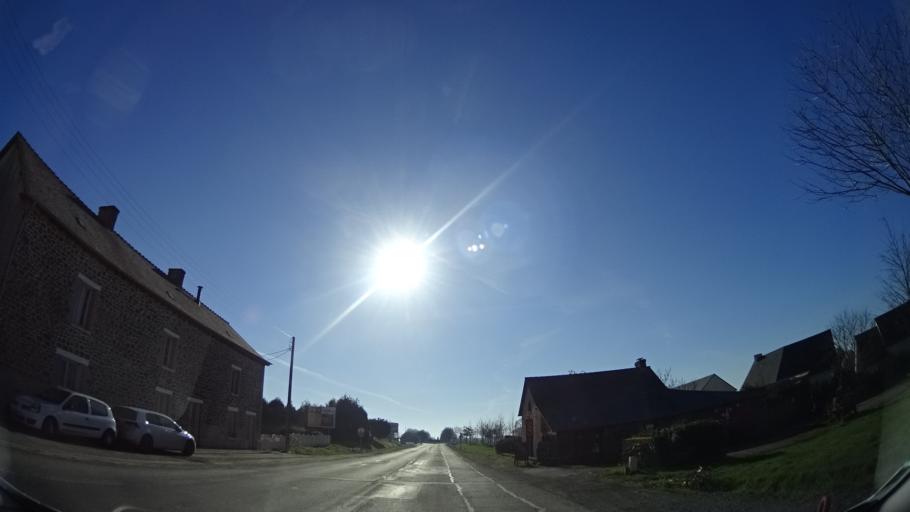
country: FR
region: Brittany
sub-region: Departement d'Ille-et-Vilaine
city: La Meziere
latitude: 48.2159
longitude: -1.7462
